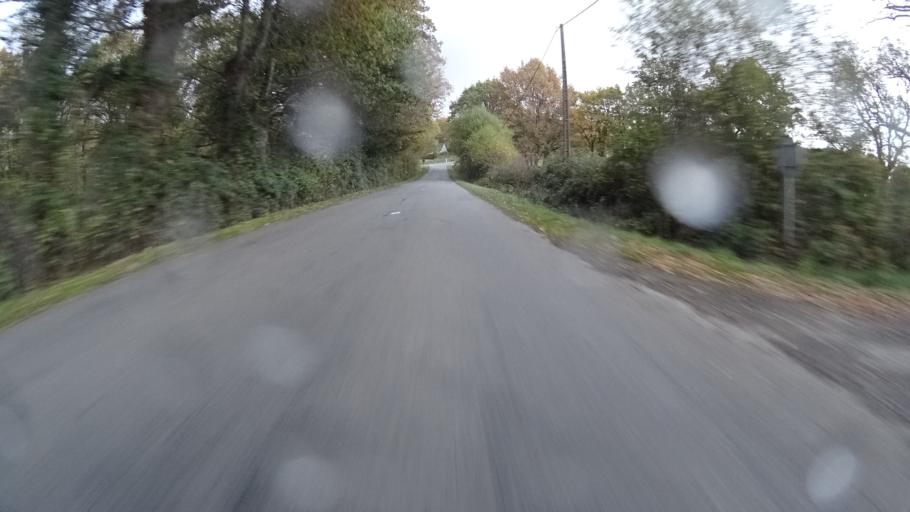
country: FR
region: Pays de la Loire
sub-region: Departement de la Loire-Atlantique
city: Saint-Nicolas-de-Redon
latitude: 47.6724
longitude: -2.0541
